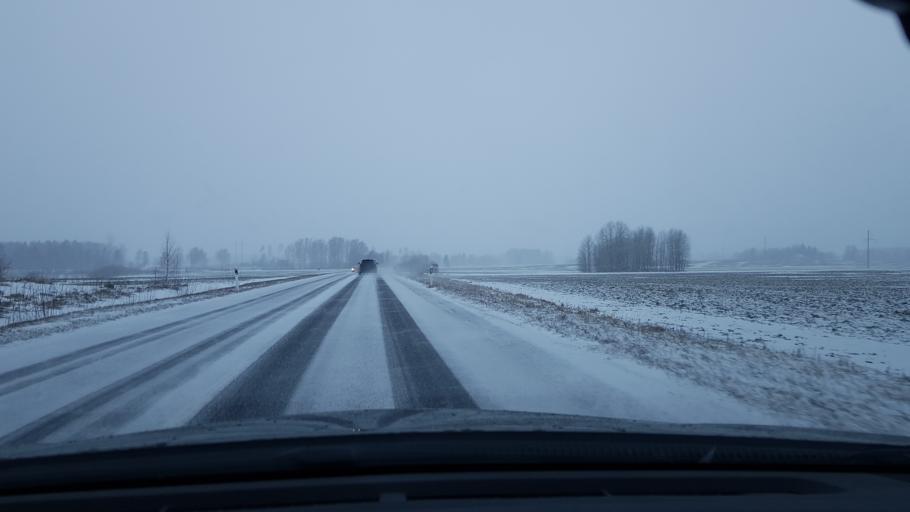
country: EE
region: Harju
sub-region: Anija vald
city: Kehra
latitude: 59.2416
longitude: 25.3652
